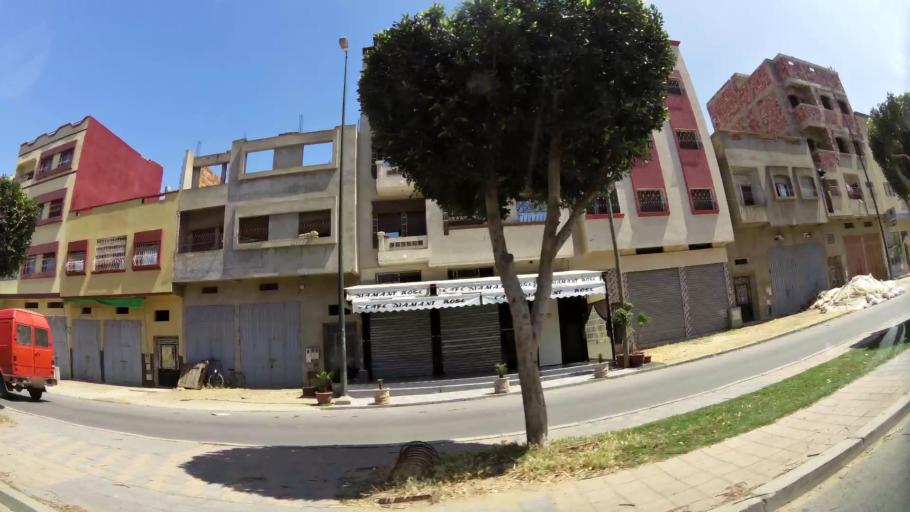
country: MA
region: Gharb-Chrarda-Beni Hssen
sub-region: Kenitra Province
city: Kenitra
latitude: 34.2435
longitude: -6.5434
